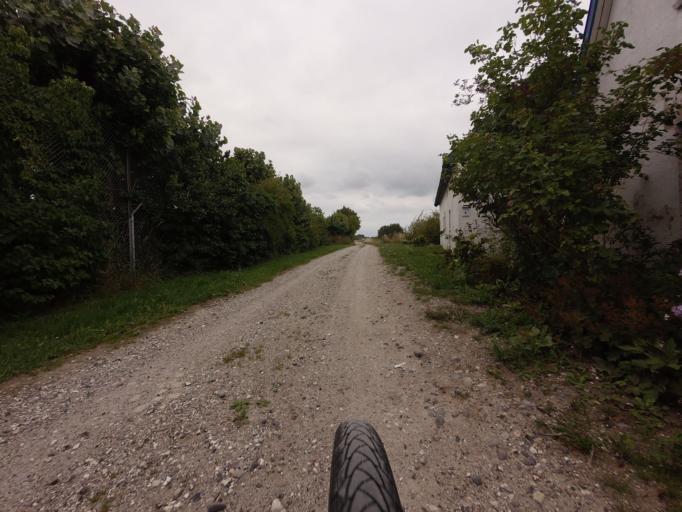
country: DK
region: Zealand
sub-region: Stevns Kommune
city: Store Heddinge
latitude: 55.3301
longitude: 12.4495
